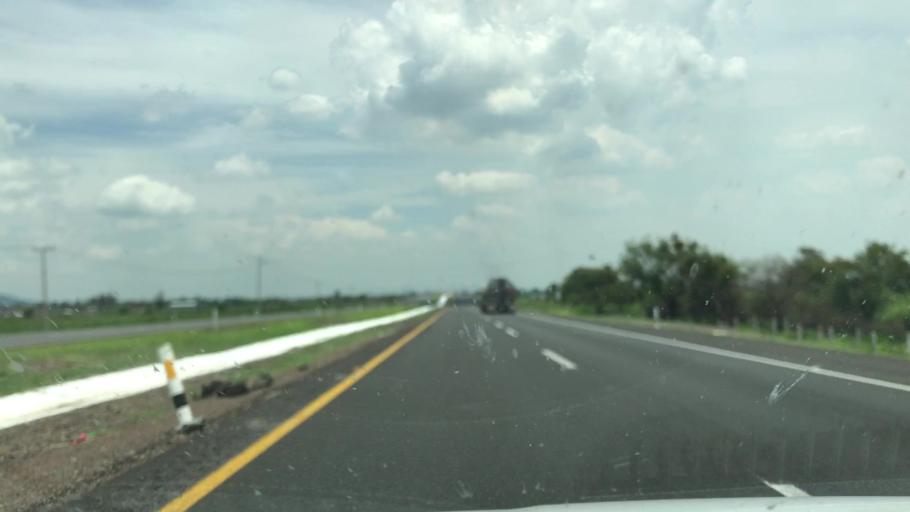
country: MX
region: Guanajuato
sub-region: Salamanca
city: San Vicente de Flores
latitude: 20.6155
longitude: -101.2265
